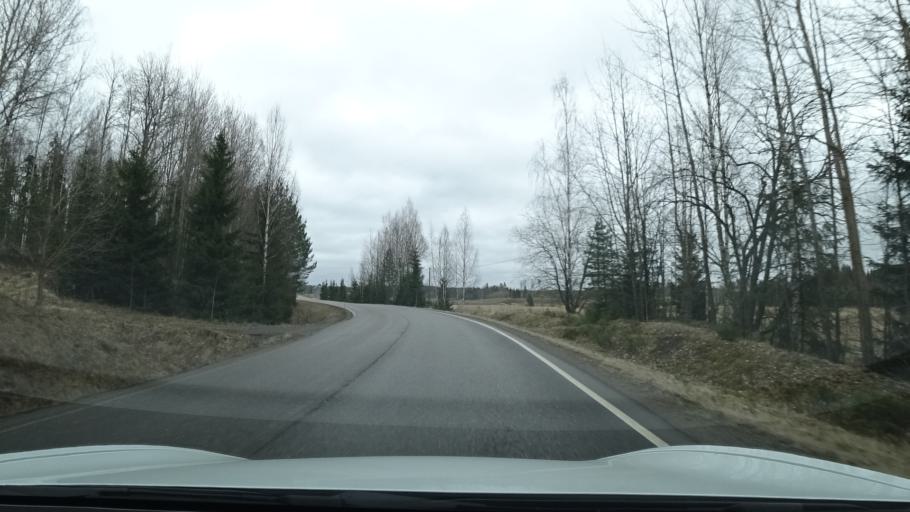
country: FI
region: Uusimaa
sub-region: Helsinki
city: Pornainen
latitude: 60.4846
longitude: 25.4331
